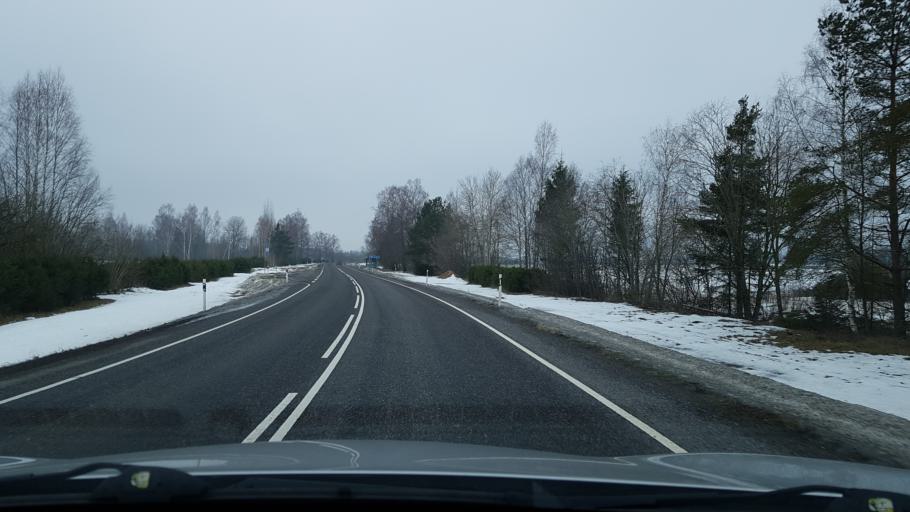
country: EE
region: Valgamaa
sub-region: Valga linn
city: Valga
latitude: 57.8565
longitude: 26.1687
